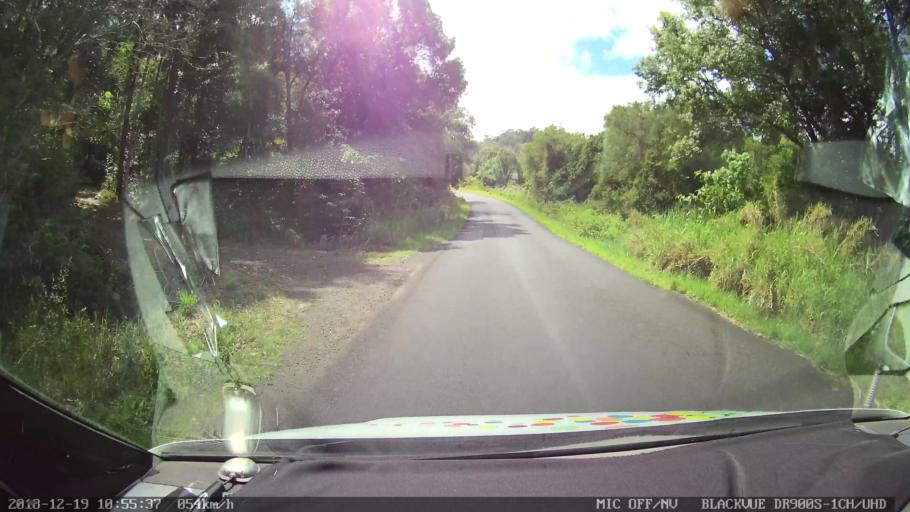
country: AU
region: New South Wales
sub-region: Lismore Municipality
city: Nimbin
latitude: -28.5956
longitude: 153.2556
